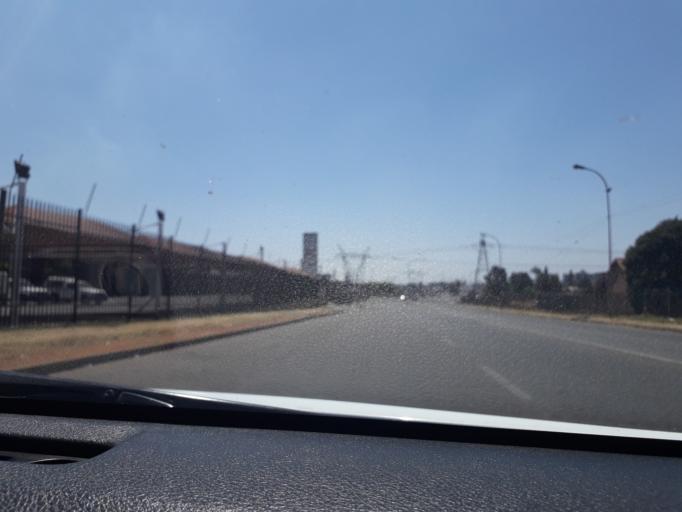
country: ZA
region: Gauteng
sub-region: City of Johannesburg Metropolitan Municipality
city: Modderfontein
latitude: -26.1135
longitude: 28.2222
